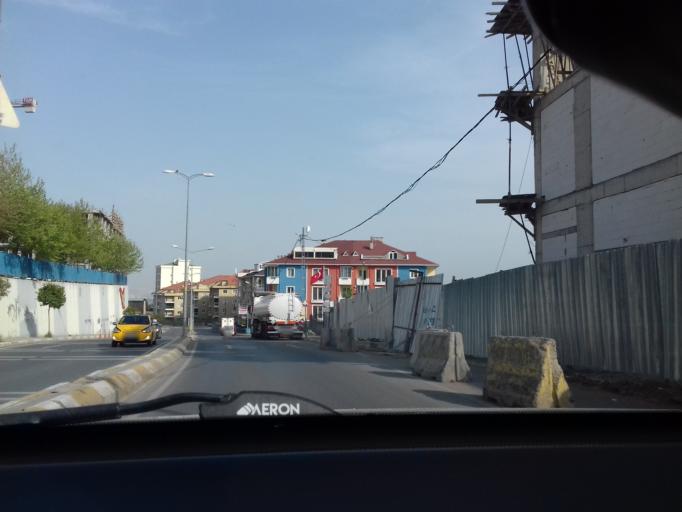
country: TR
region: Istanbul
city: Pendik
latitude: 40.9055
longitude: 29.2642
